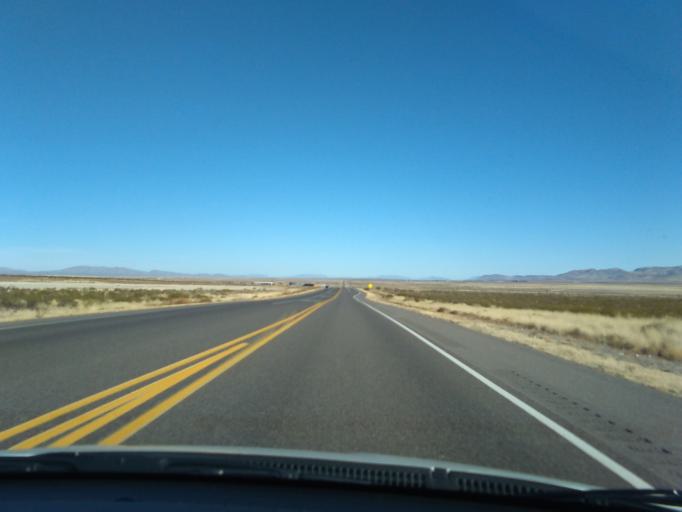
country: US
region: New Mexico
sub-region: Dona Ana County
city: Hatch
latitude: 32.5782
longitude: -107.3903
